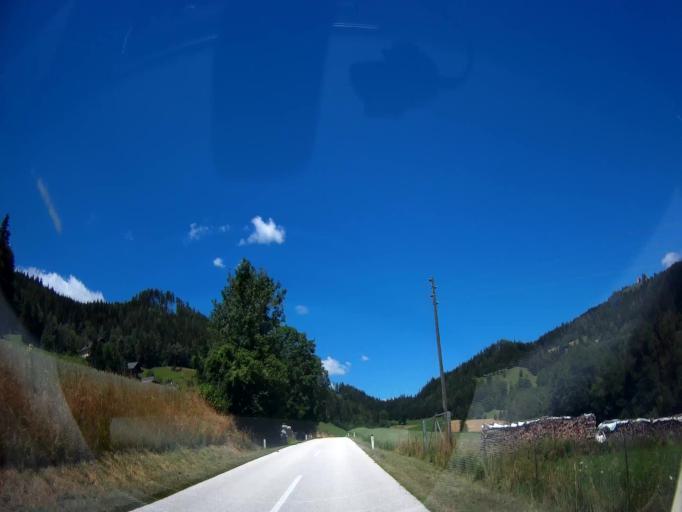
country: AT
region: Carinthia
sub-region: Politischer Bezirk Sankt Veit an der Glan
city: St. Georgen am Laengsee
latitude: 46.7189
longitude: 14.4158
